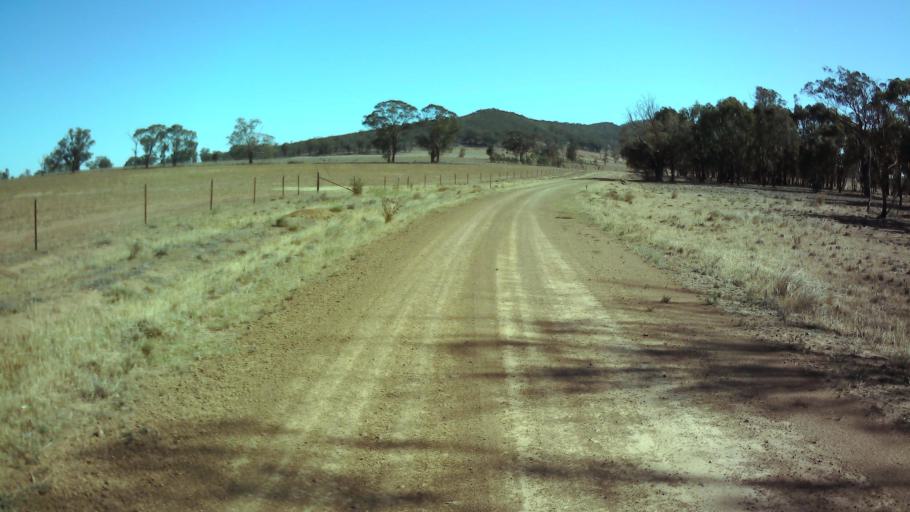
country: AU
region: New South Wales
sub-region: Weddin
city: Grenfell
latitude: -33.7656
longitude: 147.9235
